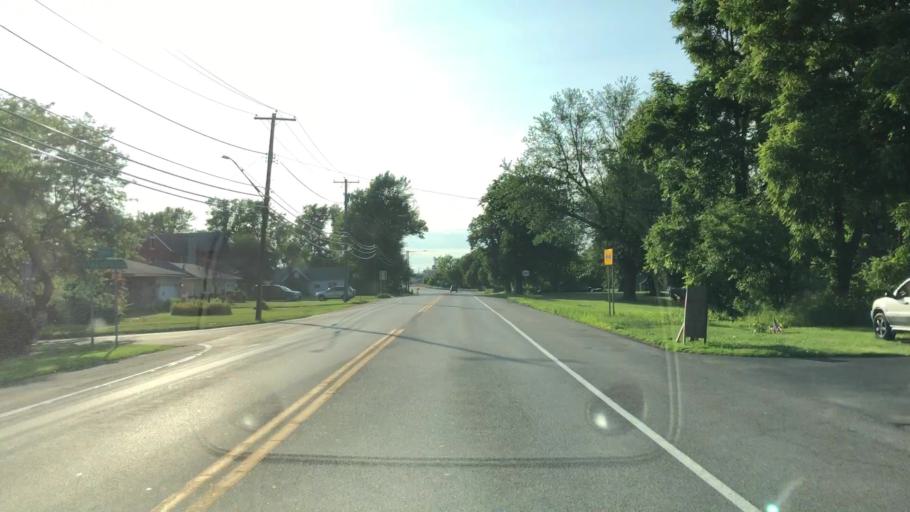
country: US
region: New York
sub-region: Erie County
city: Sloan
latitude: 42.8696
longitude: -78.7794
